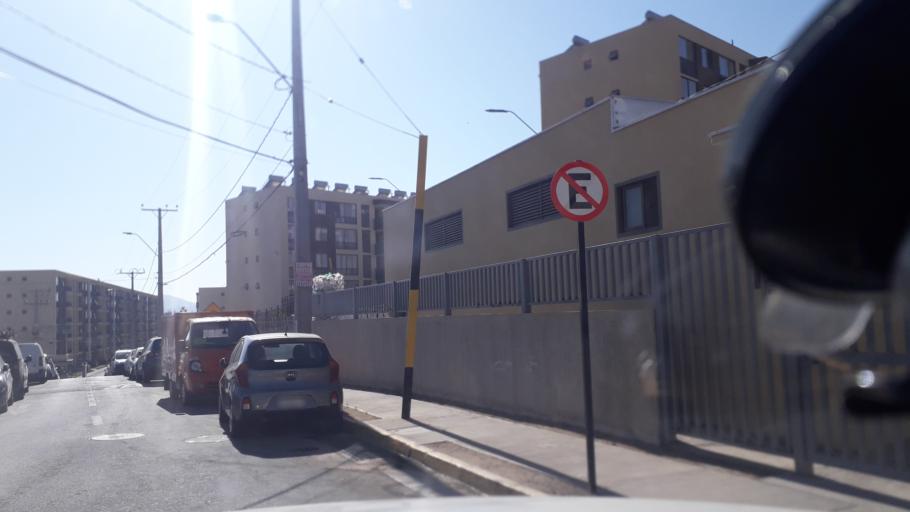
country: CL
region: Valparaiso
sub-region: Provincia de Marga Marga
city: Quilpue
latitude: -33.0667
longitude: -71.4176
